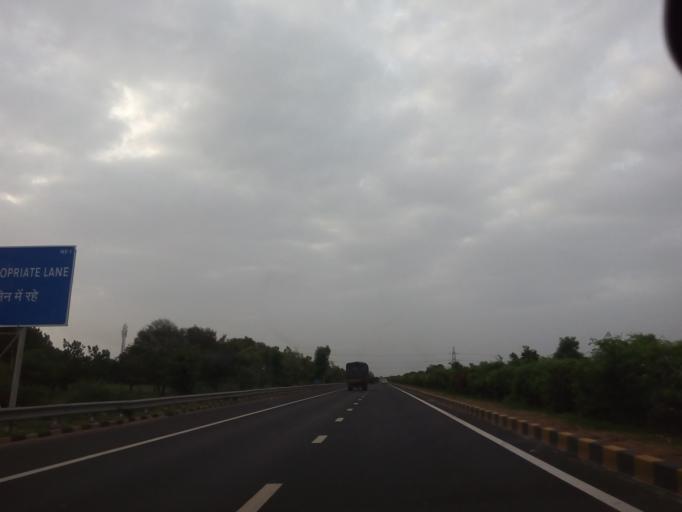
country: IN
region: Gujarat
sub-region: Kheda
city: Mahemdavad
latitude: 22.9376
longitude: 72.7193
